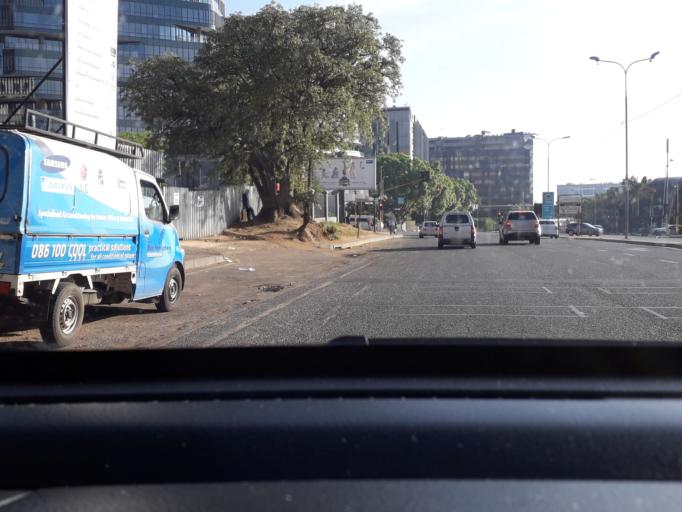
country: ZA
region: Gauteng
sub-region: City of Johannesburg Metropolitan Municipality
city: Johannesburg
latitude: -26.1109
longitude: 28.0569
